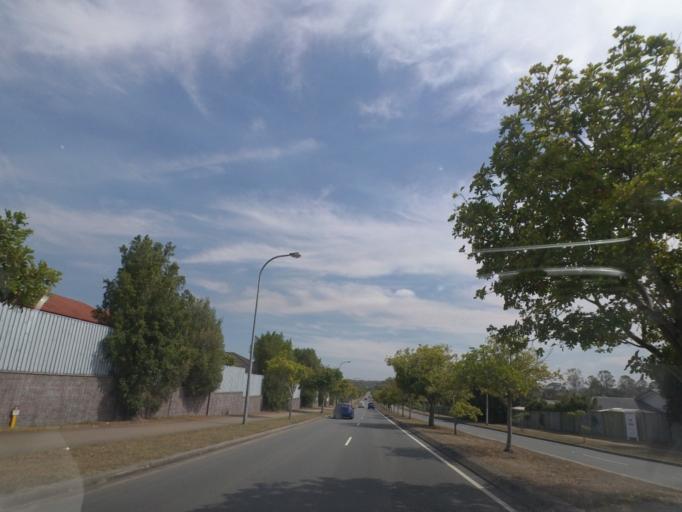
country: AU
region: Queensland
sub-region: Brisbane
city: Sunnybank Hills
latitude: -27.6263
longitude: 153.0594
